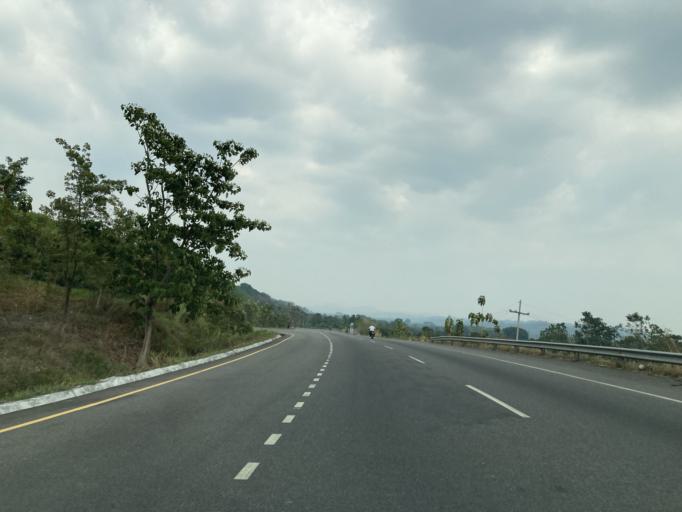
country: GT
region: Suchitepeque
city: San Juan Bautista
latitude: 14.3962
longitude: -91.2167
